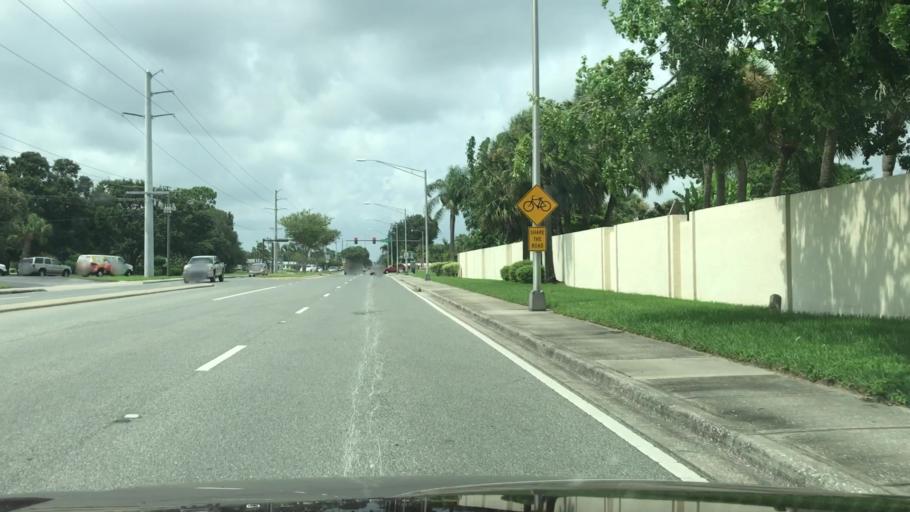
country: US
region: Florida
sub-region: Sarasota County
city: Gulf Gate Estates
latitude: 27.2546
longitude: -82.4975
